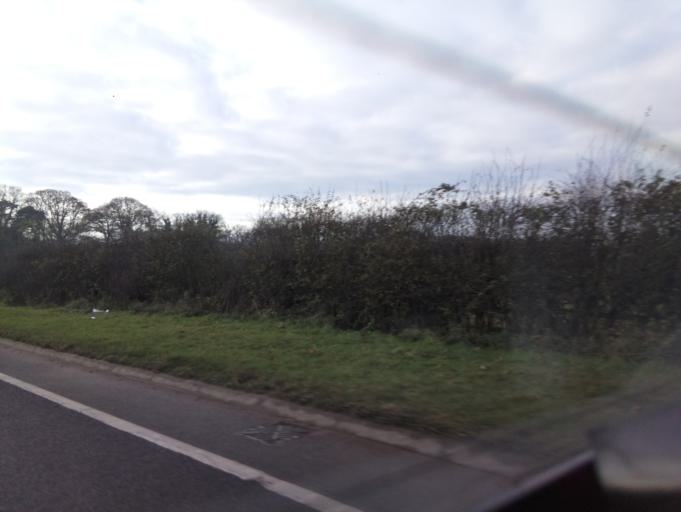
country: GB
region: England
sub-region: Staffordshire
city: Shenstone
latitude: 52.6347
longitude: -1.8026
